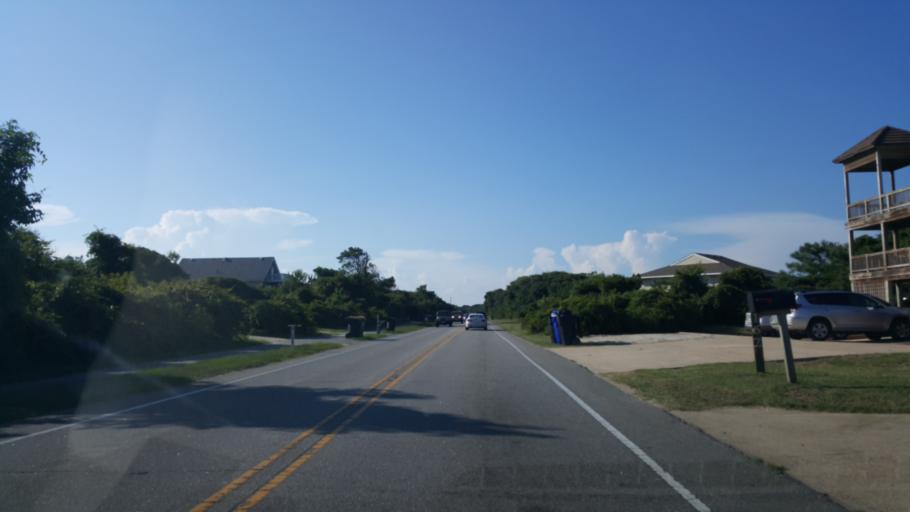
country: US
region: North Carolina
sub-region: Dare County
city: Southern Shores
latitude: 36.1231
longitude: -75.7264
